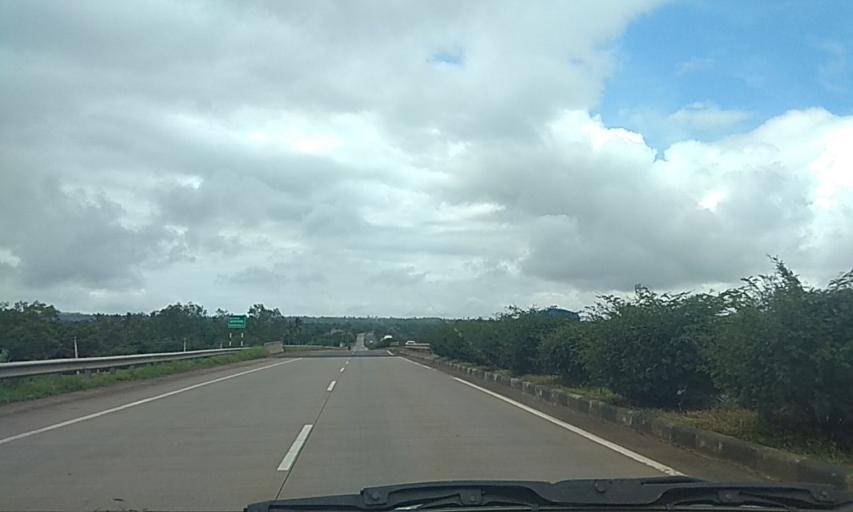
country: IN
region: Karnataka
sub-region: Belgaum
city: Sankeshwar
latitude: 16.3139
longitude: 74.4274
